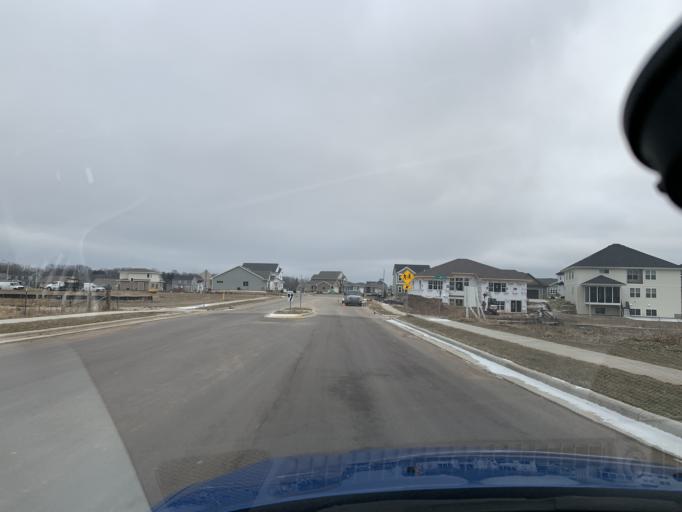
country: US
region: Wisconsin
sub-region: Dane County
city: Middleton
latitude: 43.0715
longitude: -89.5618
